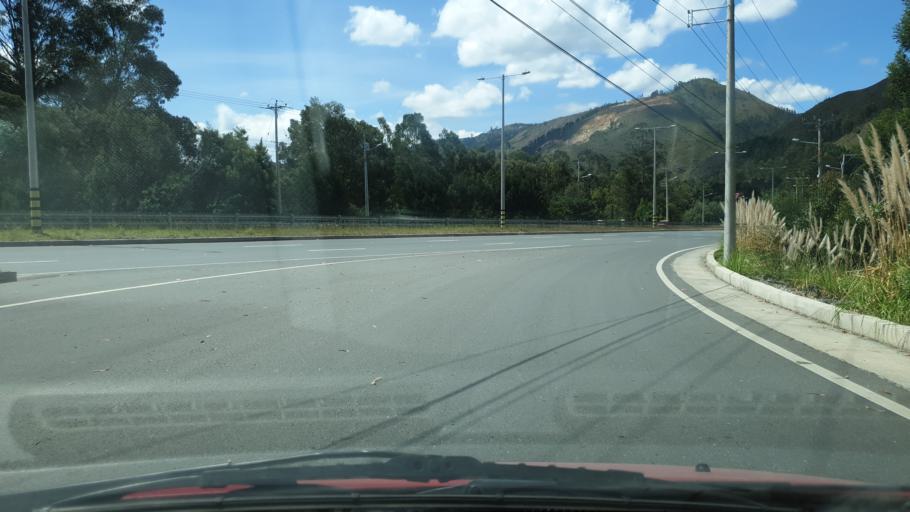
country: EC
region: Azuay
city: Llacao
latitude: -2.8445
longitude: -78.8810
